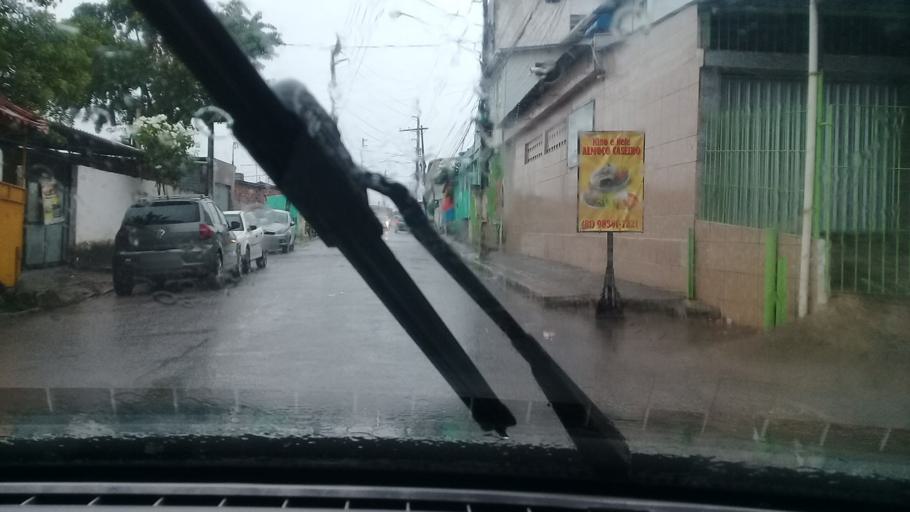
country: BR
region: Pernambuco
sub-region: Paulista
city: Paulista
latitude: -7.9628
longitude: -34.8903
